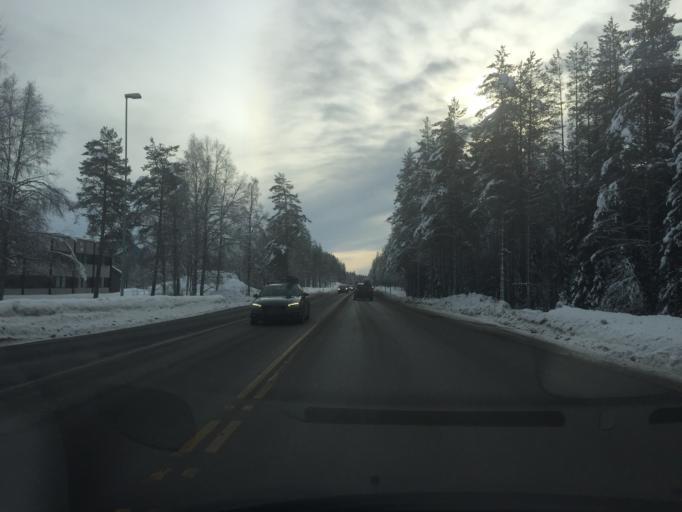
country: NO
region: Hedmark
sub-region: Trysil
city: Innbygda
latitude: 61.2942
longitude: 12.2706
